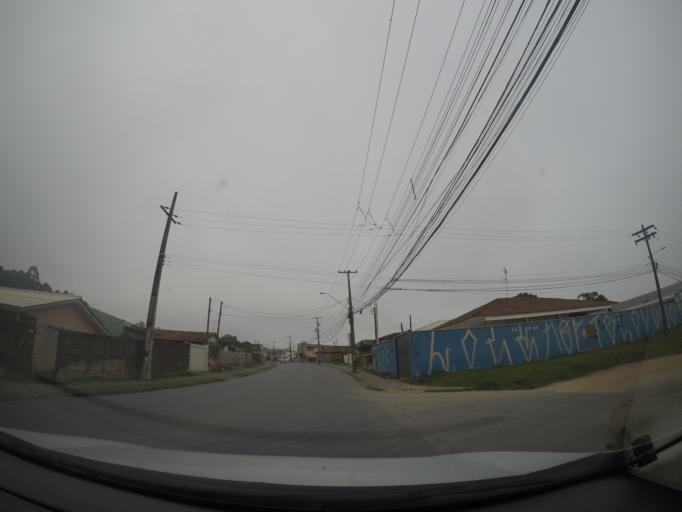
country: BR
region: Parana
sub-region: Almirante Tamandare
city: Almirante Tamandare
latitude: -25.3460
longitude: -49.2615
